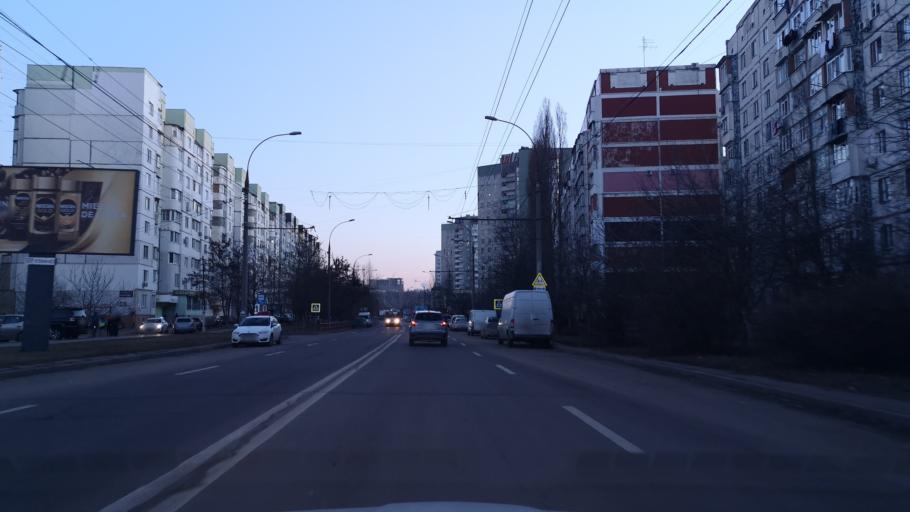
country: MD
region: Chisinau
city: Stauceni
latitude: 47.0573
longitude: 28.8481
